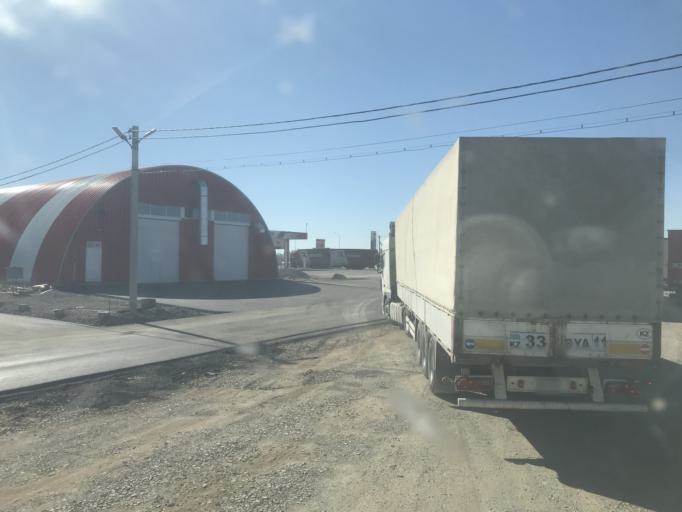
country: KZ
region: Aqtoebe
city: Aqtobe
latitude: 50.2964
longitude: 57.4764
